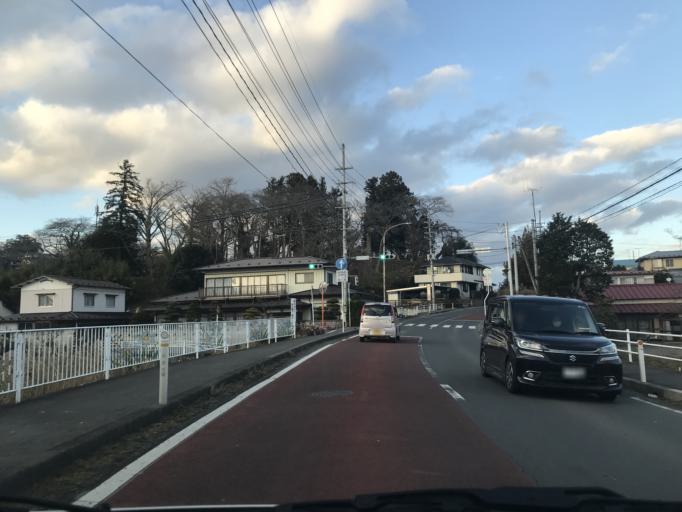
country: JP
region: Miyagi
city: Furukawa
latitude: 38.6608
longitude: 141.0109
